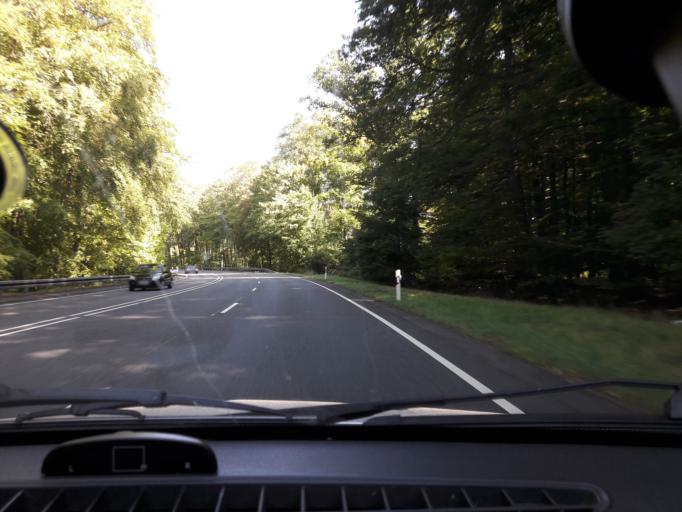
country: DE
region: Hesse
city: Taunusstein
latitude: 50.1177
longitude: 8.1795
